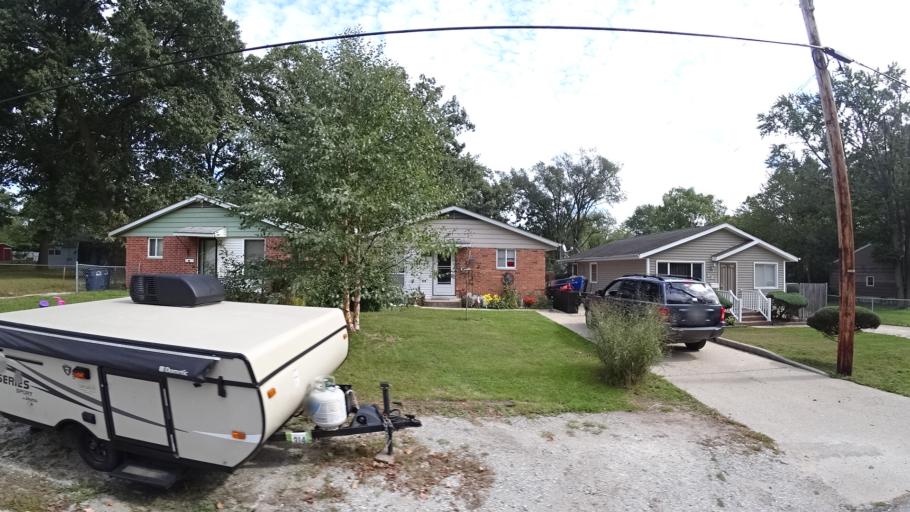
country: US
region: Indiana
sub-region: LaPorte County
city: Trail Creek
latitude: 41.7104
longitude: -86.8672
